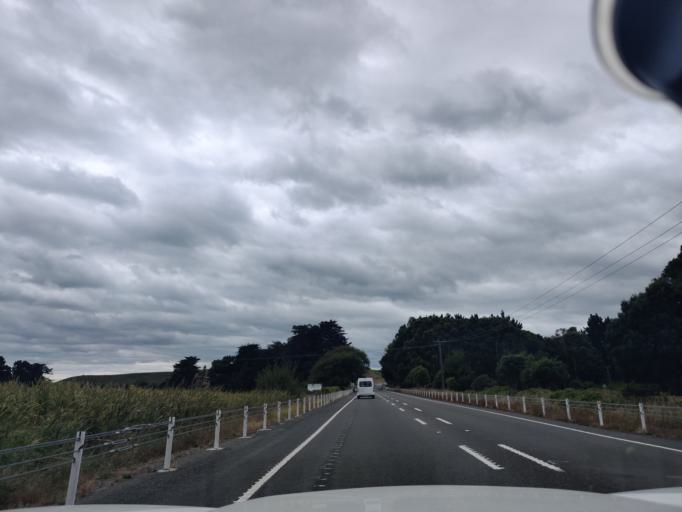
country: NZ
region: Manawatu-Wanganui
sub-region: Horowhenua District
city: Levin
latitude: -40.5948
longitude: 175.3404
